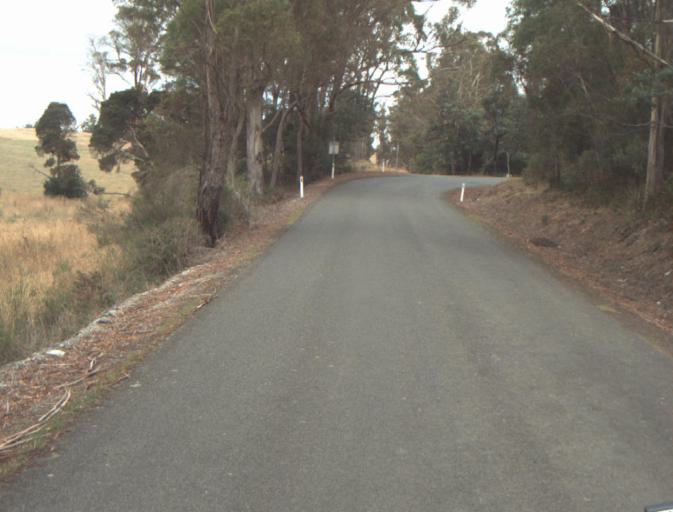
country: AU
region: Tasmania
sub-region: Launceston
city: Mayfield
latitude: -41.2387
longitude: 147.1968
